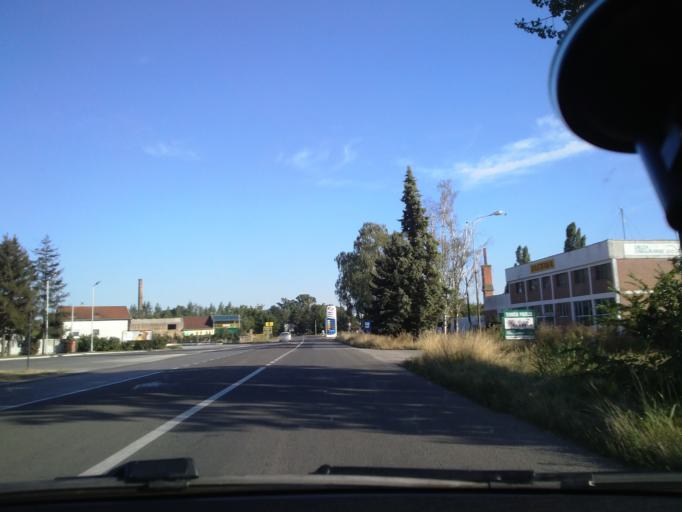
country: RS
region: Autonomna Pokrajina Vojvodina
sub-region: Zapadnobacki Okrug
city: Odzaci
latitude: 45.5163
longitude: 19.2475
